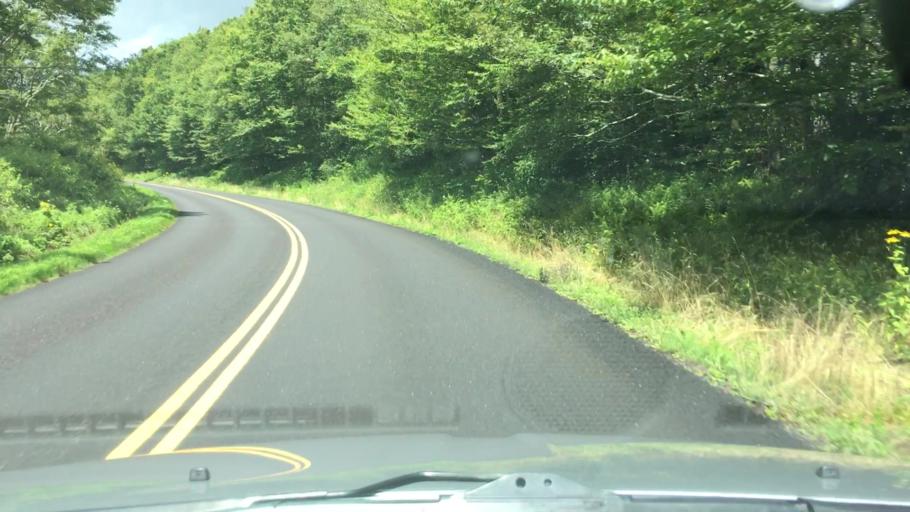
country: US
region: North Carolina
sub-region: Buncombe County
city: Black Mountain
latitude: 35.7428
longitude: -82.3382
